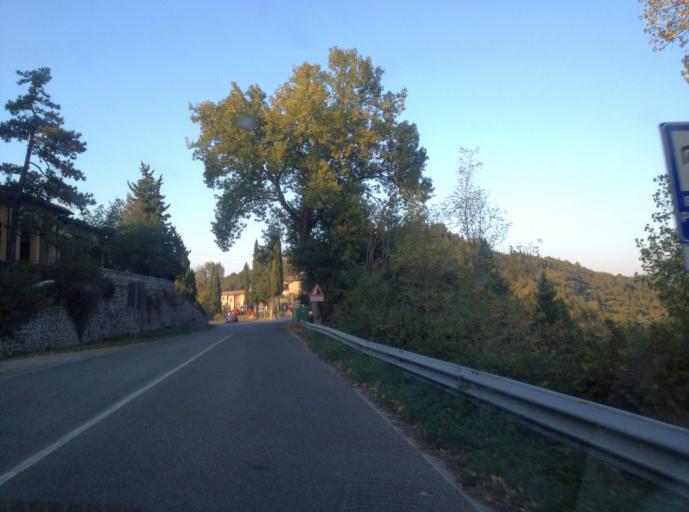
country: IT
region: Tuscany
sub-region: Provincia di Siena
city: Castellina in Chianti
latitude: 43.4901
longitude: 11.3001
